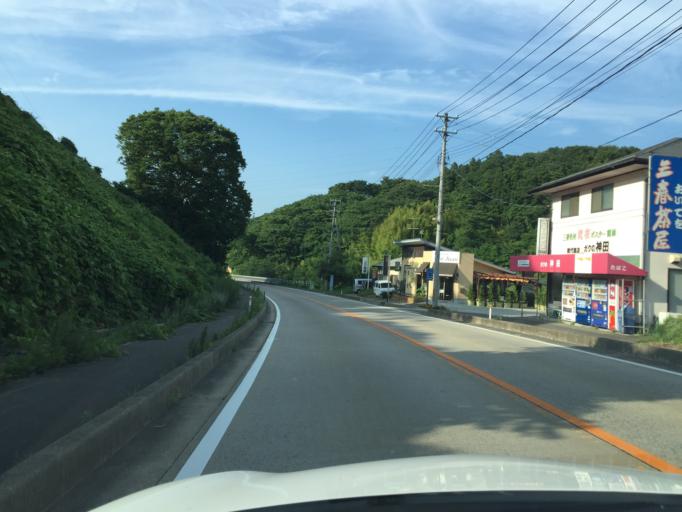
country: JP
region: Fukushima
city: Miharu
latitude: 37.4370
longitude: 140.5015
